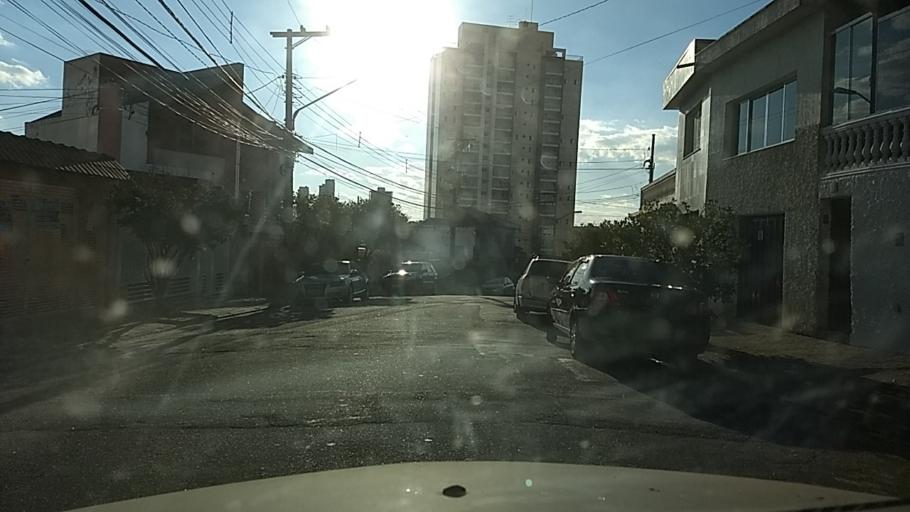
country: BR
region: Sao Paulo
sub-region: Sao Paulo
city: Sao Paulo
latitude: -23.5072
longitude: -46.5941
